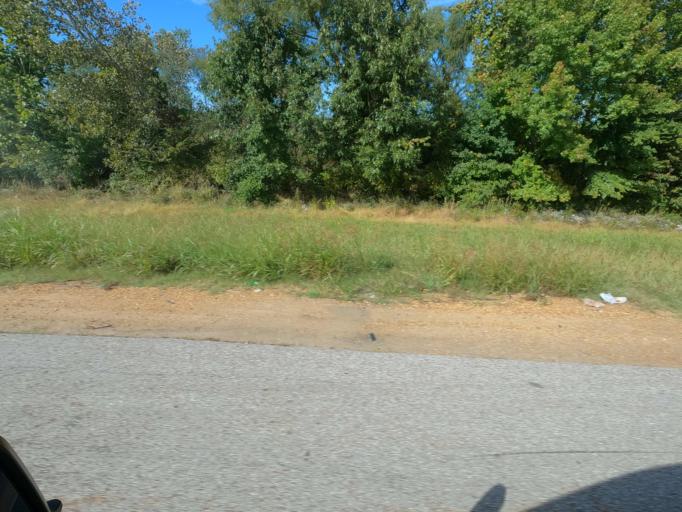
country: US
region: Tennessee
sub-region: Shelby County
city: Arlington
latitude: 35.2648
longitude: -89.6608
